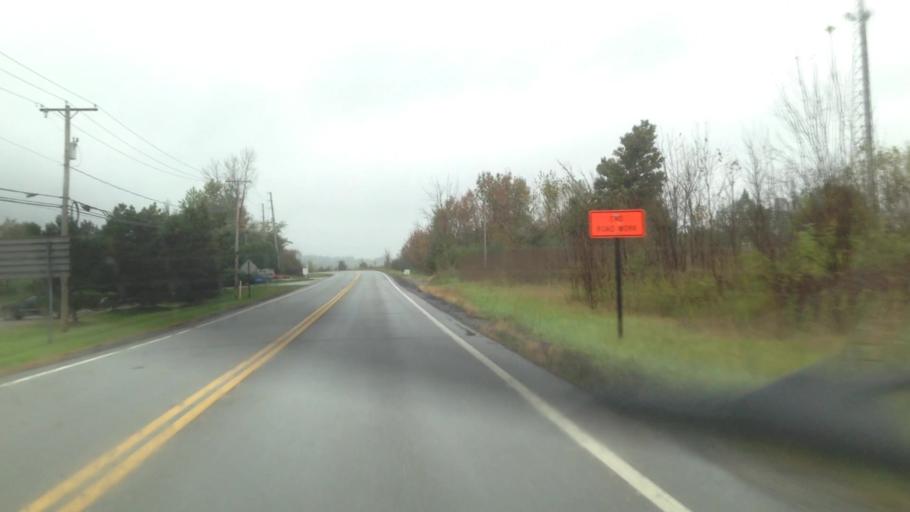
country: US
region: Ohio
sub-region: Portage County
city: Streetsboro
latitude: 41.2622
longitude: -81.3809
